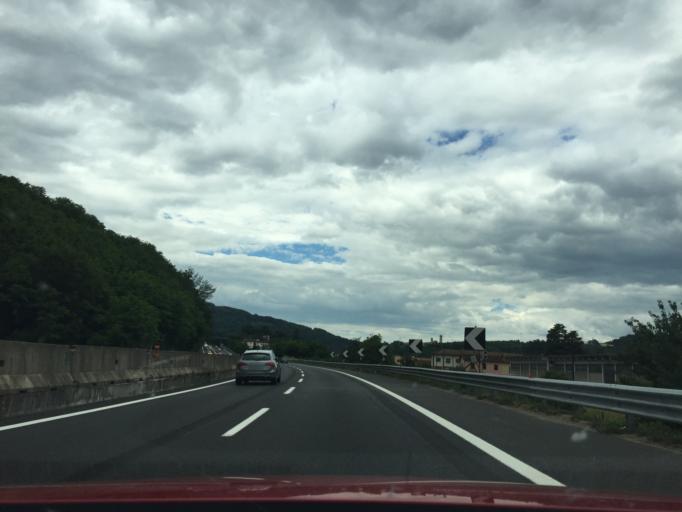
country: IT
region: Tuscany
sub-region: Provincia di Pistoia
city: Stazione Masotti
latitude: 43.9110
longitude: 10.8615
